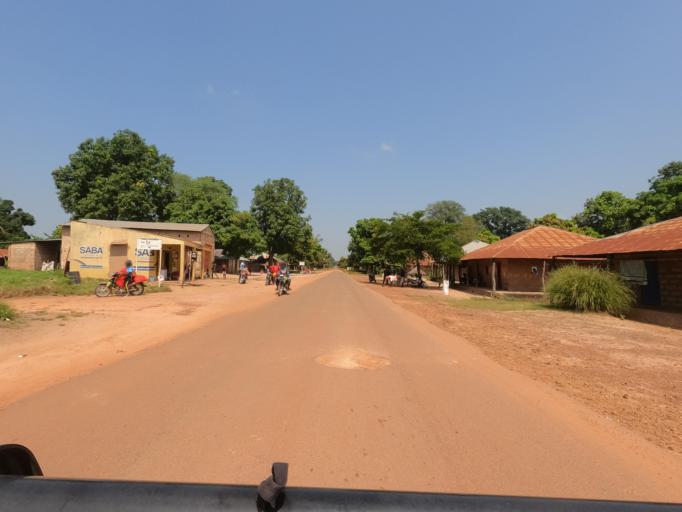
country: GW
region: Oio
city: Bissora
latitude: 12.3632
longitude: -15.7741
